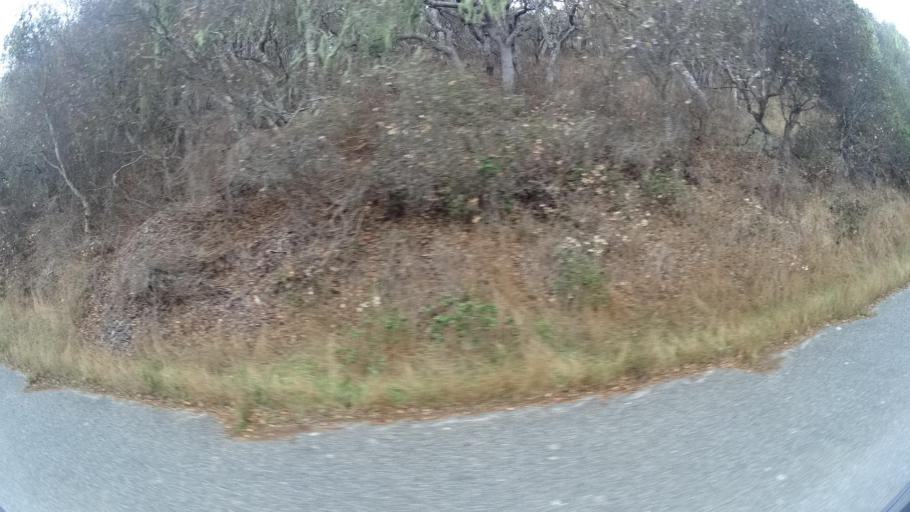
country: US
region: California
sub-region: Monterey County
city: Marina
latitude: 36.6516
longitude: -121.7480
